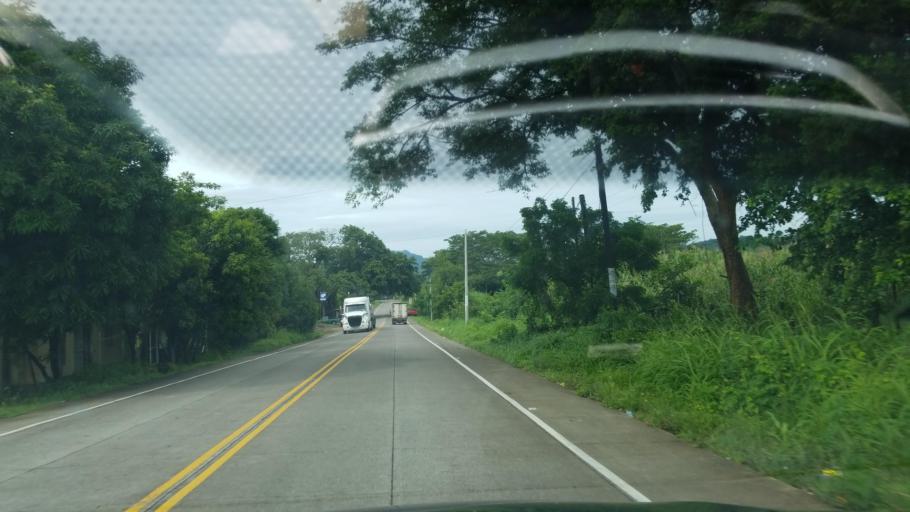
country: HN
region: Choluteca
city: Pespire
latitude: 13.6423
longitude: -87.3686
